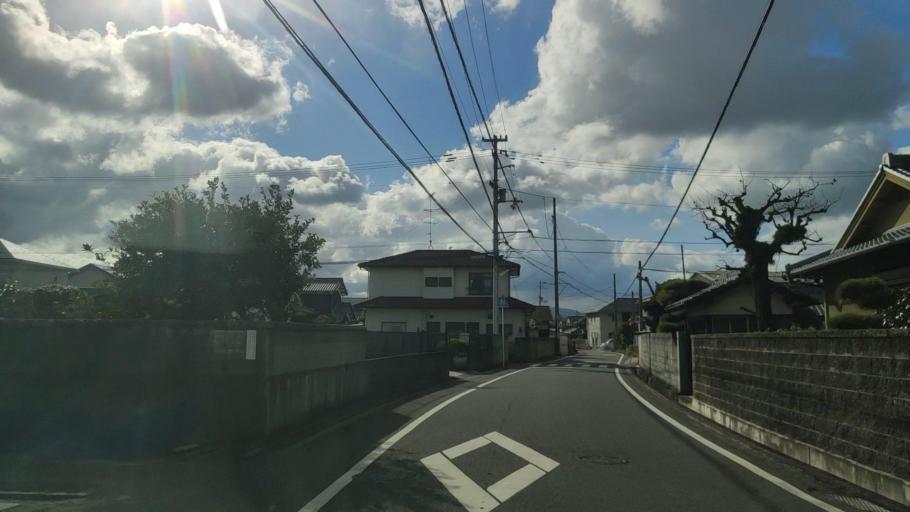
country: JP
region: Ehime
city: Masaki-cho
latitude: 33.8265
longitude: 132.7087
